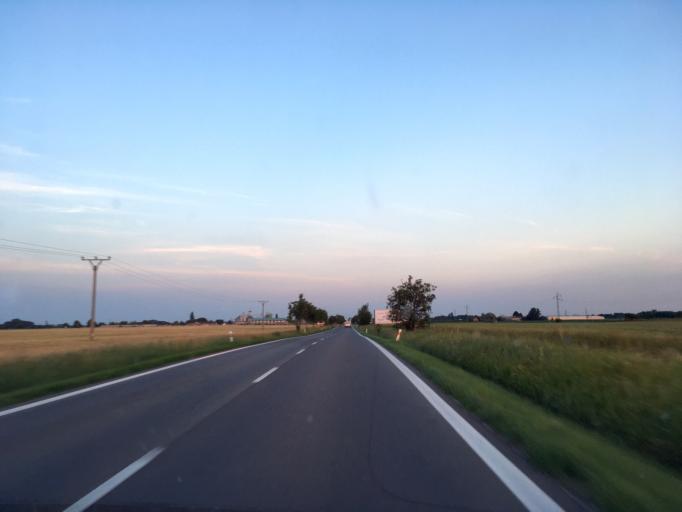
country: SK
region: Nitriansky
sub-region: Okres Nove Zamky
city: Nove Zamky
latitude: 48.0221
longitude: 18.1429
